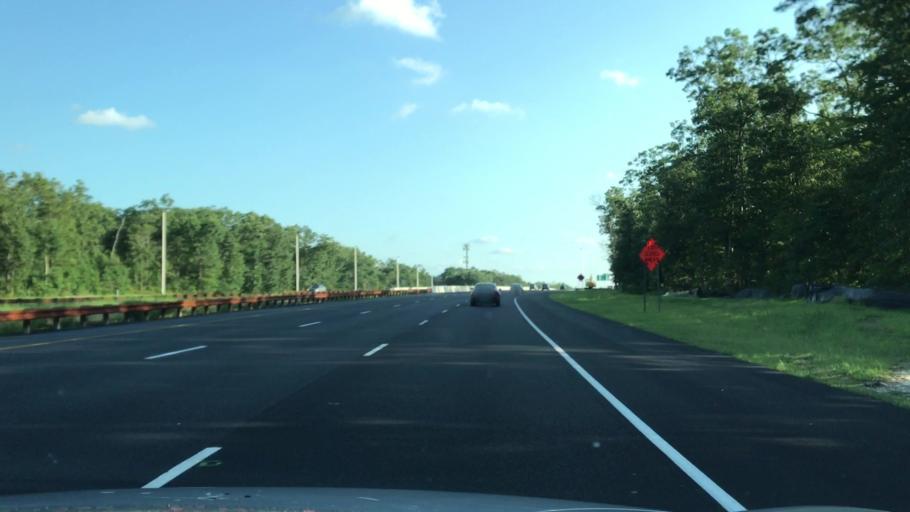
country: US
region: New Jersey
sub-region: Atlantic County
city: Pomona
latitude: 39.4550
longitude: -74.5353
